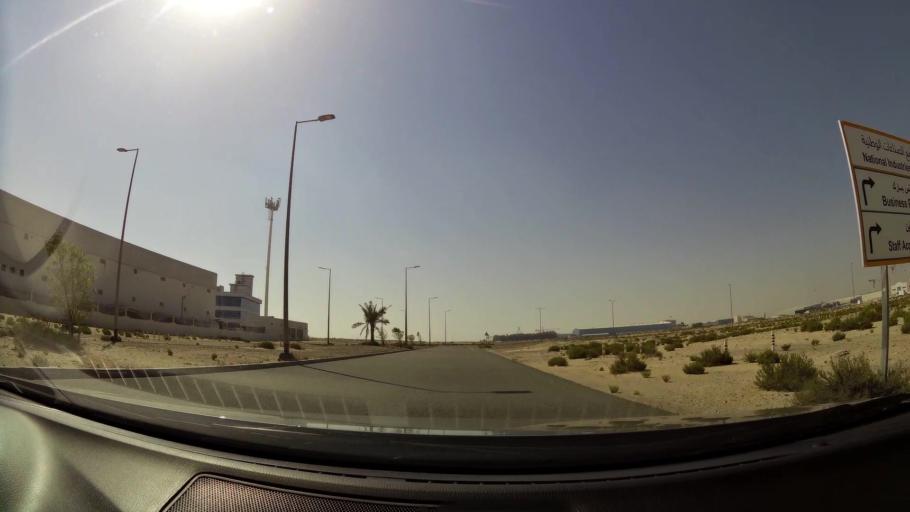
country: AE
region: Dubai
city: Dubai
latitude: 24.9271
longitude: 55.0589
